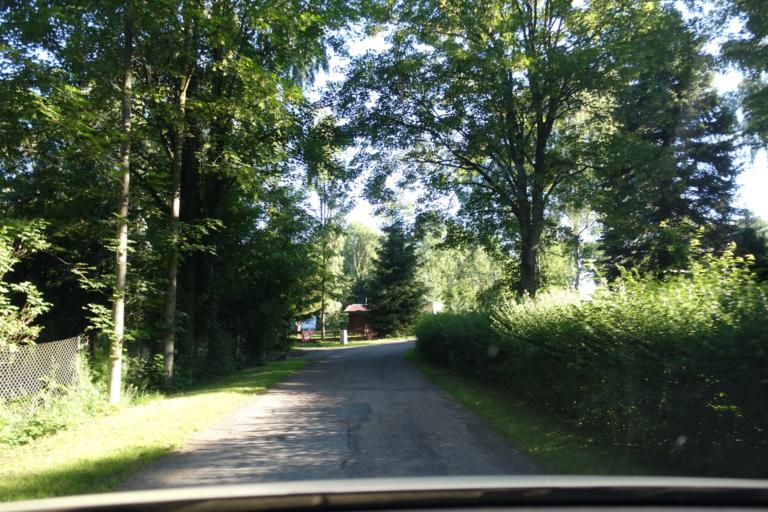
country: DE
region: Saxony
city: Brand-Erbisdorf
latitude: 50.8583
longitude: 13.2985
